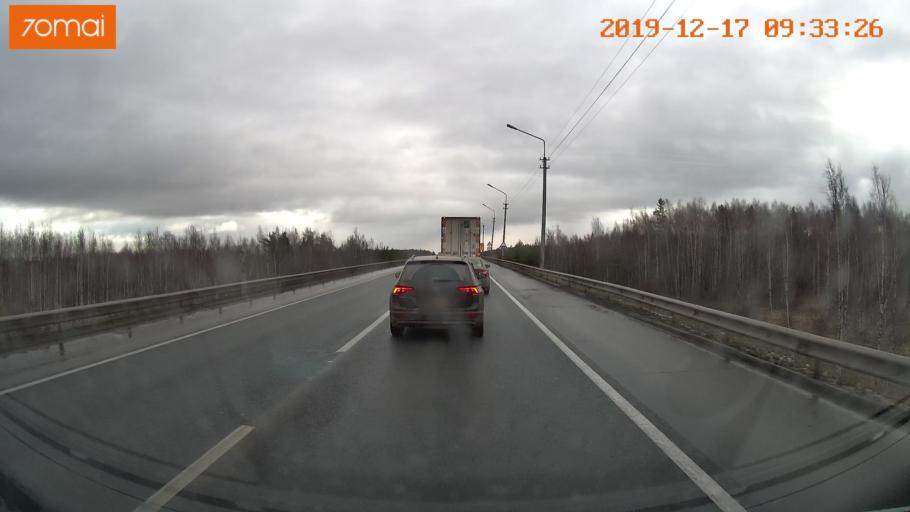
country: RU
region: Vladimir
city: Vorsha
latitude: 56.0773
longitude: 40.2083
